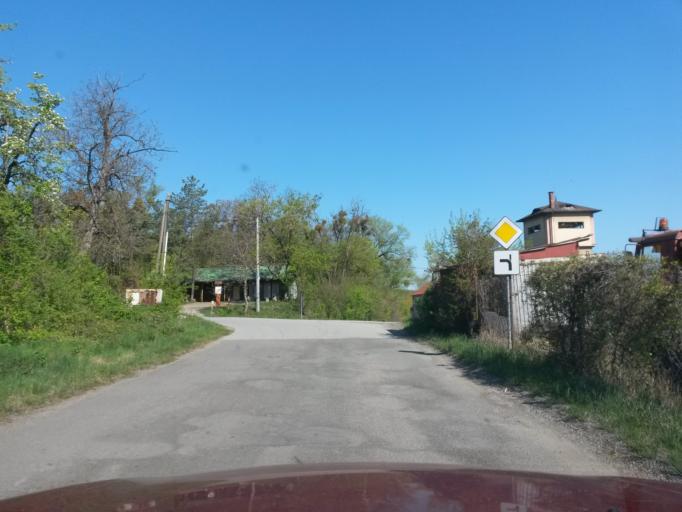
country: SK
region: Kosicky
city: Secovce
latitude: 48.6422
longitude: 21.4892
